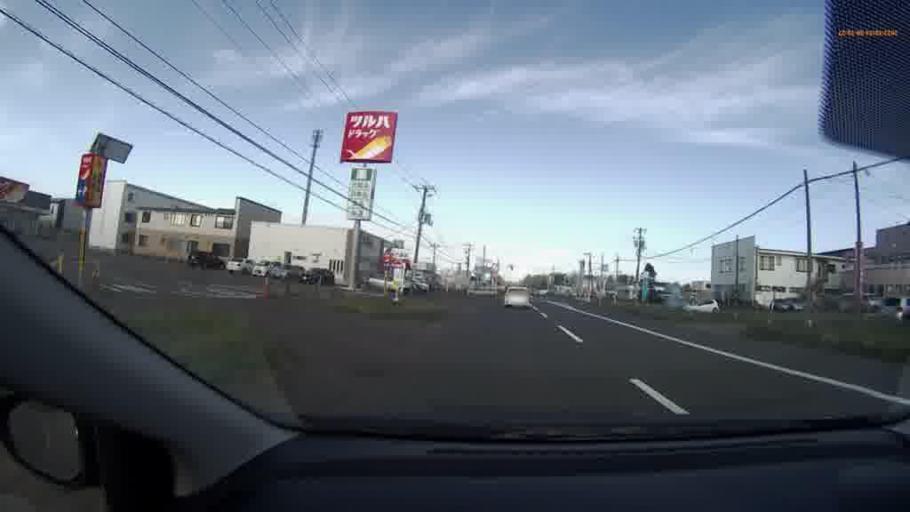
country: JP
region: Hokkaido
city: Kushiro
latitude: 43.0119
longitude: 144.4086
